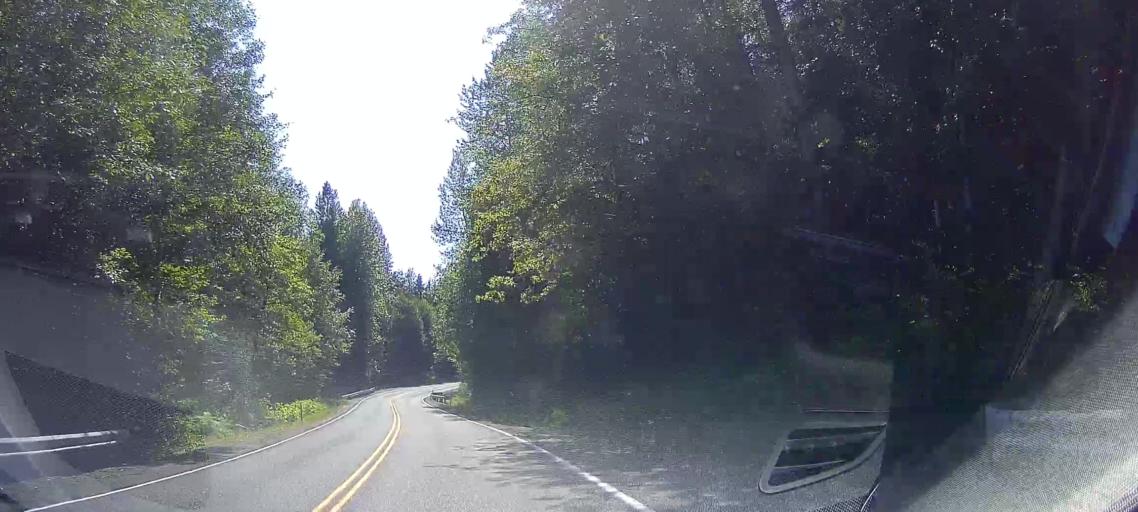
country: US
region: Washington
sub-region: Snohomish County
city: Bryant
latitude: 48.3336
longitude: -122.1316
